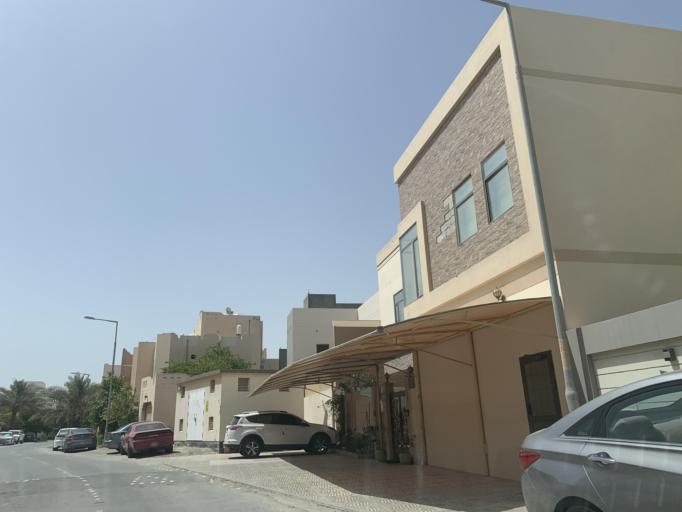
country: BH
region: Northern
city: Sitrah
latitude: 26.1572
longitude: 50.5883
